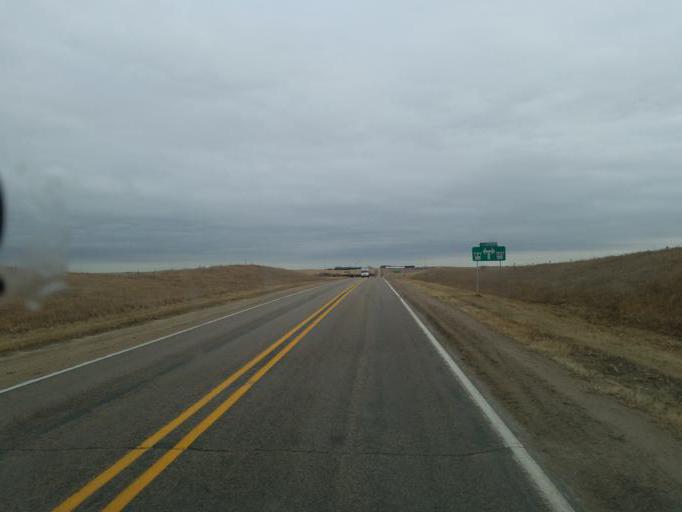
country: US
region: Nebraska
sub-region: Knox County
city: Bloomfield
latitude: 42.5979
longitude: -97.5289
